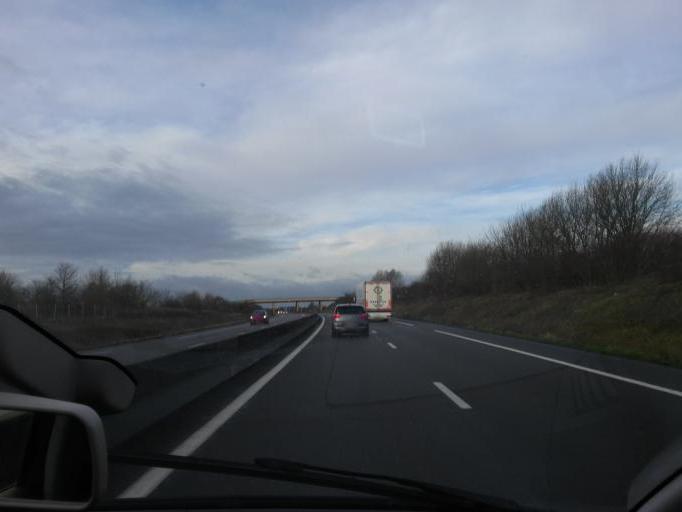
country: FR
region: Picardie
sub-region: Departement de la Somme
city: Chaulnes
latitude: 49.8577
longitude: 2.7850
